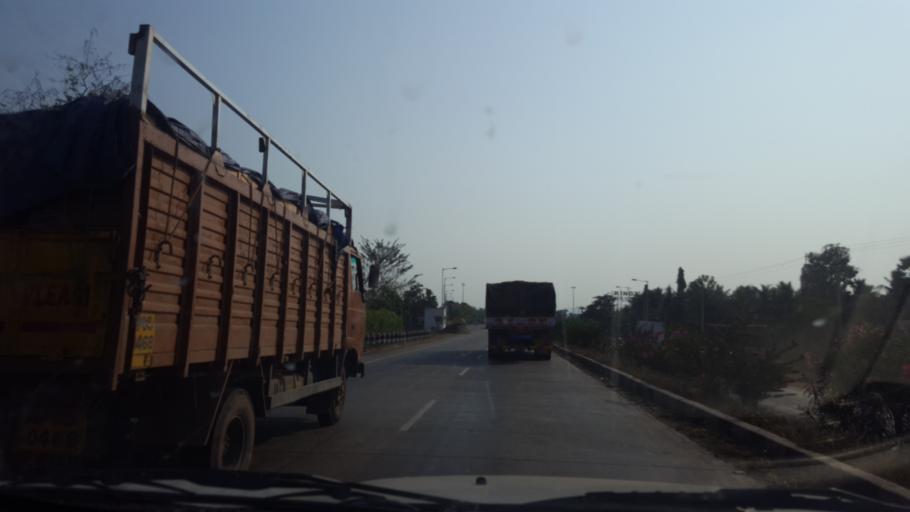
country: IN
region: Andhra Pradesh
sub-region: Vishakhapatnam
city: Elamanchili
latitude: 17.5901
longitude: 82.8702
